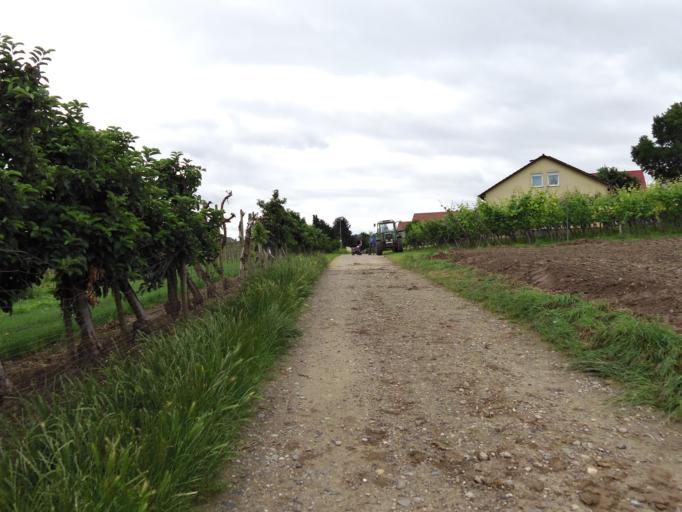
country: DE
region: Rheinland-Pfalz
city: Dirmstein
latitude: 49.5706
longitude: 8.2434
